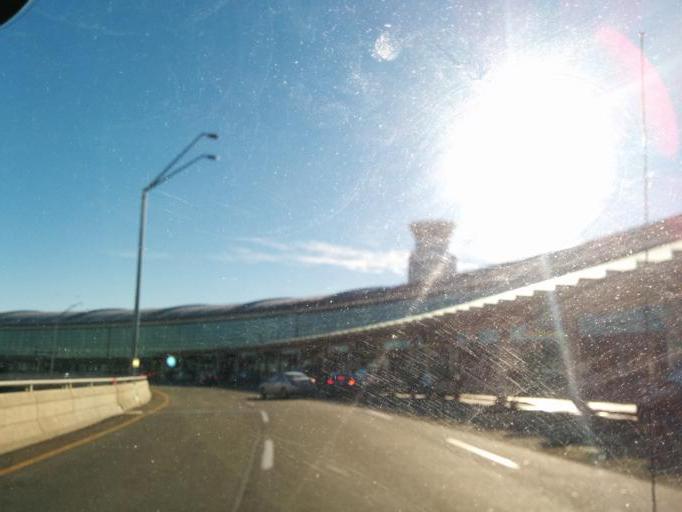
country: CA
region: Ontario
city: Etobicoke
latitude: 43.6827
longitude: -79.6137
